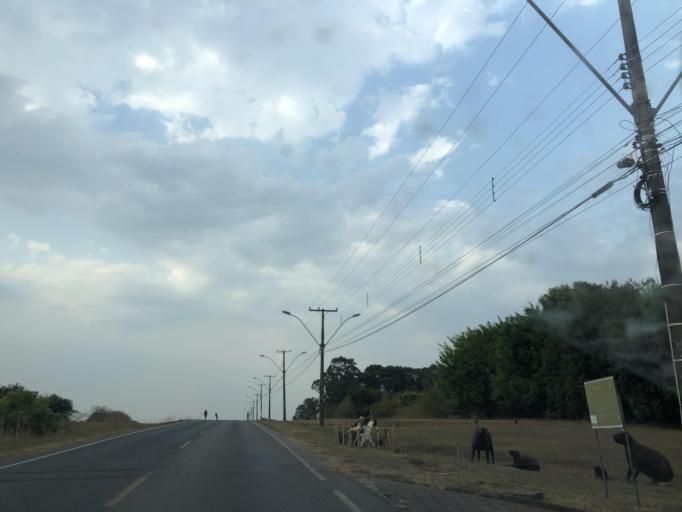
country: BR
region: Federal District
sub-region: Brasilia
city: Brasilia
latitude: -15.9318
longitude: -47.9732
